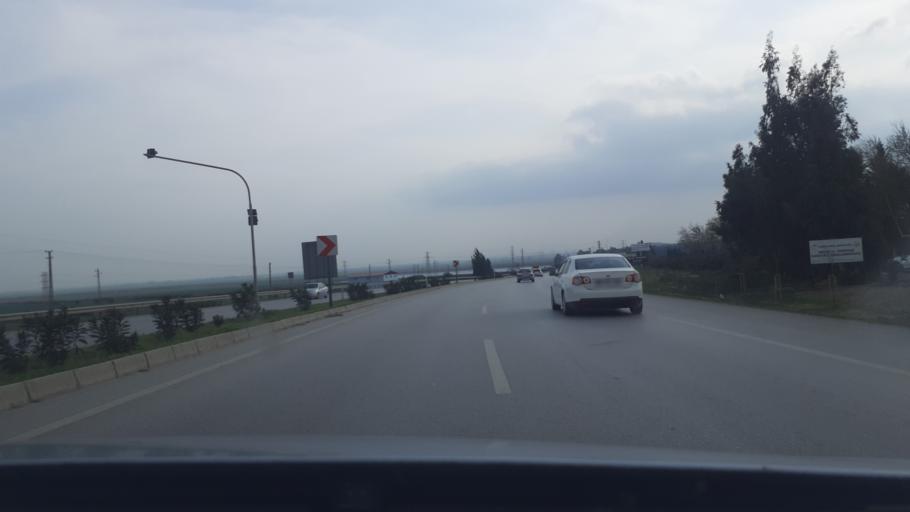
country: TR
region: Hatay
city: Kirikhan
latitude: 36.4410
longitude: 36.2833
